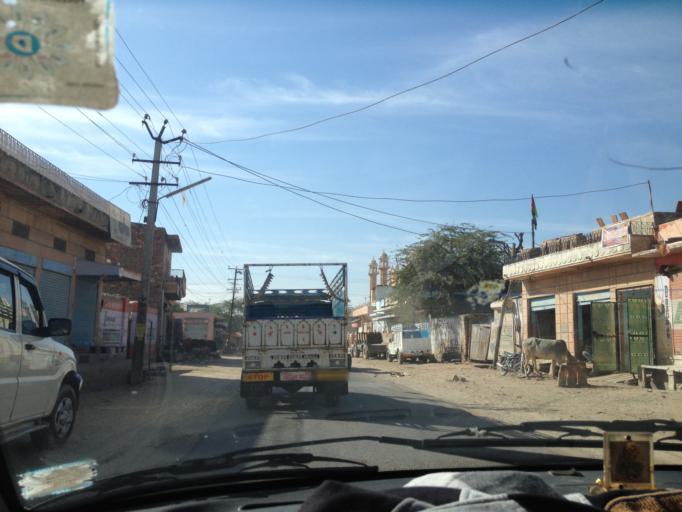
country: IN
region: Rajasthan
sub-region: Nagaur
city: Merta
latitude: 26.6473
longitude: 74.0282
